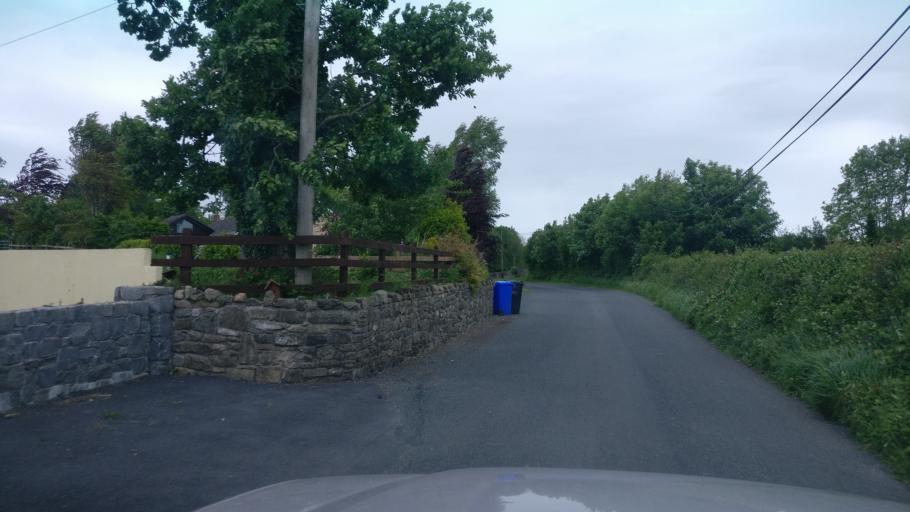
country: IE
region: Connaught
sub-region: County Galway
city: Portumna
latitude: 53.1063
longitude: -8.3981
